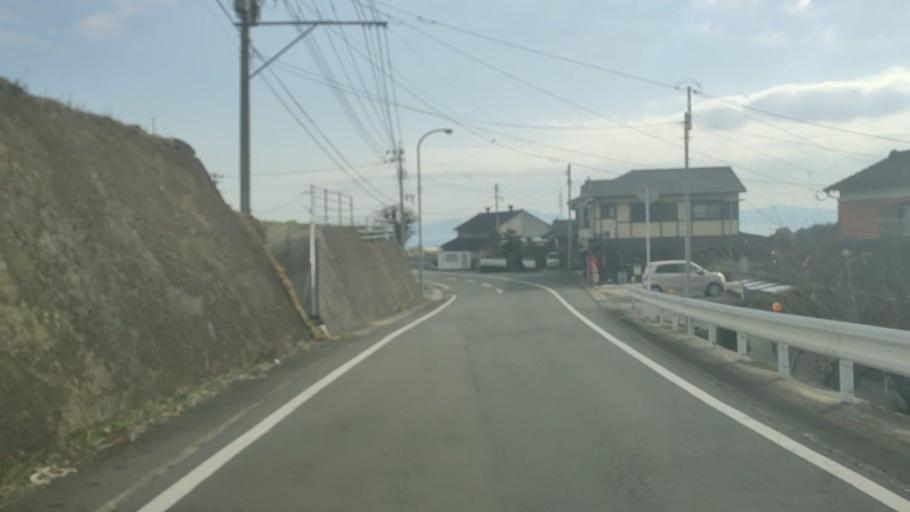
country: JP
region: Nagasaki
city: Shimabara
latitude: 32.6718
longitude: 130.2826
